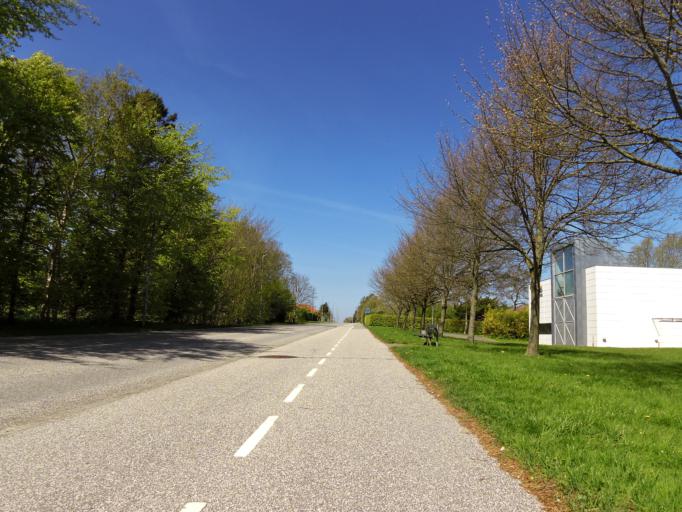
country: DK
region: Central Jutland
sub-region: Struer Kommune
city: Struer
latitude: 56.5068
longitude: 8.5798
